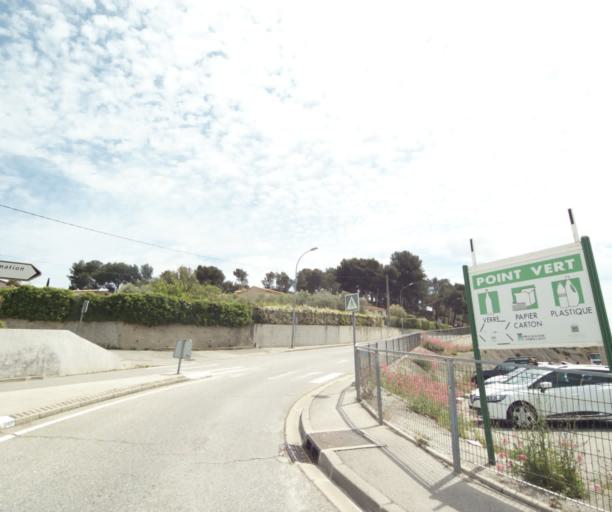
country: FR
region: Provence-Alpes-Cote d'Azur
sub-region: Departement des Bouches-du-Rhone
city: Rognac
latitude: 43.4917
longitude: 5.2335
